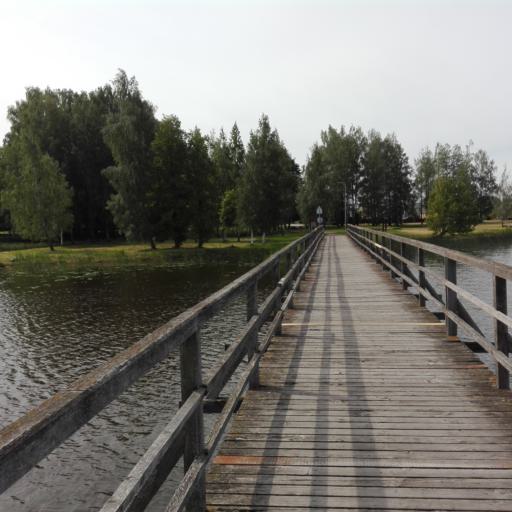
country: LT
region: Panevezys
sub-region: Birzai
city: Birzai
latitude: 56.2127
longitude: 24.7694
